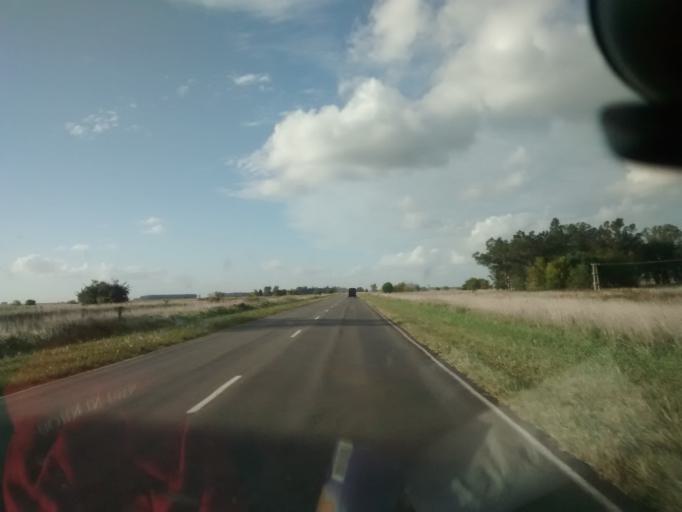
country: AR
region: Buenos Aires
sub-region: Partido de Ayacucho
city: Ayacucho
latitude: -36.6478
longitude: -58.5735
